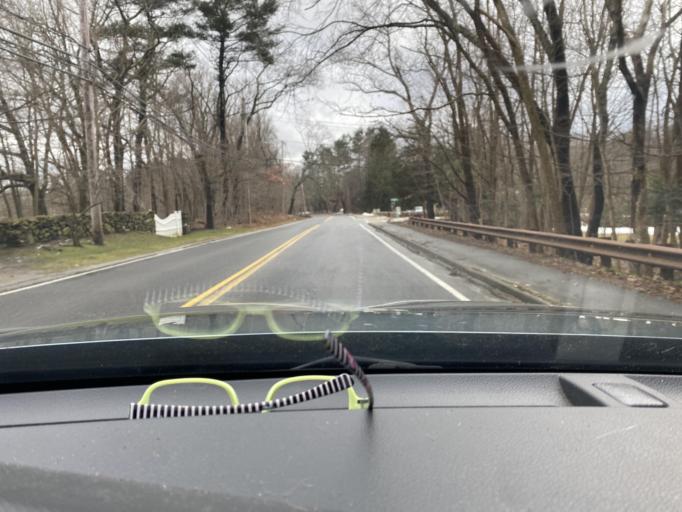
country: US
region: Massachusetts
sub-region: Middlesex County
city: Sherborn
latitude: 42.2329
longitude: -71.3673
